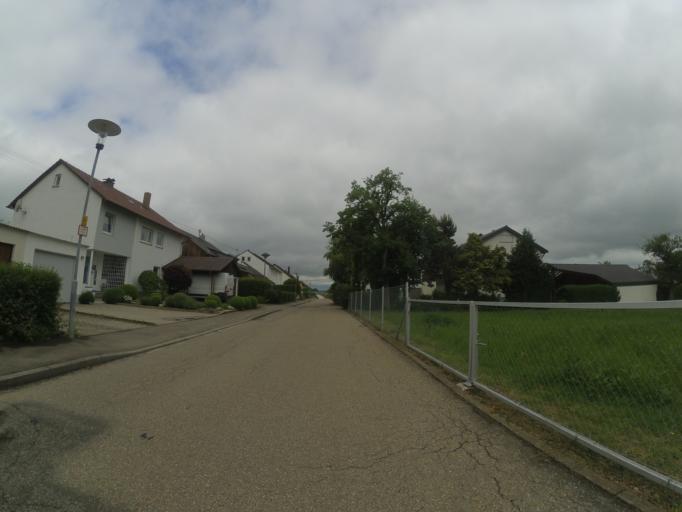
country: DE
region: Baden-Wuerttemberg
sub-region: Tuebingen Region
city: Bernstadt
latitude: 48.4971
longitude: 10.0256
